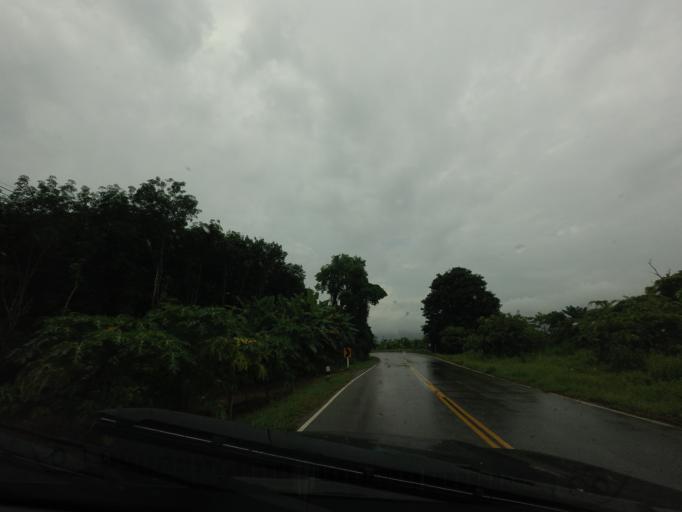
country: TH
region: Nong Khai
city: Sangkhom
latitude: 18.2122
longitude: 102.0927
